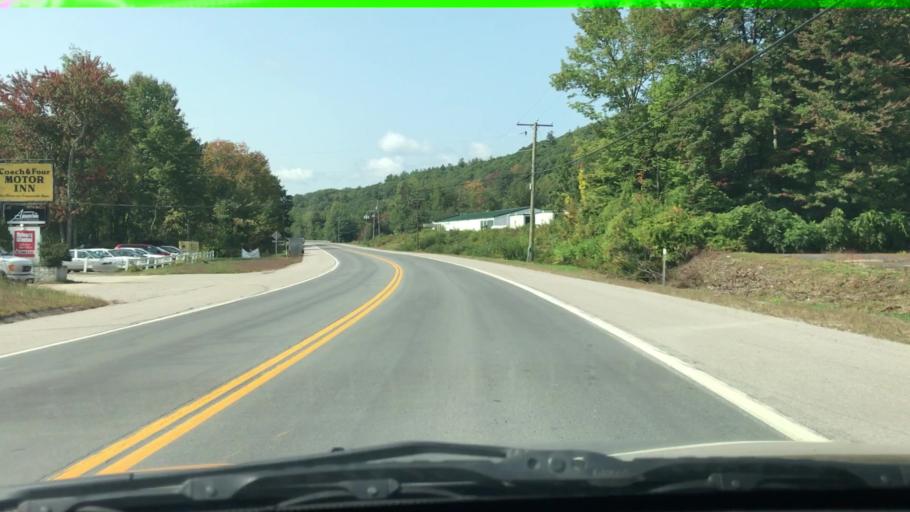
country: US
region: New Hampshire
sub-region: Cheshire County
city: Marlborough
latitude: 42.8730
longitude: -72.2167
